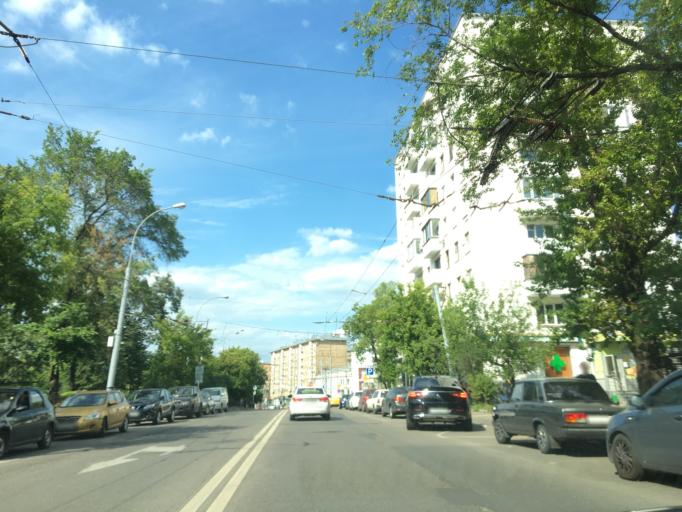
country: RU
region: Moskovskaya
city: Dorogomilovo
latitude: 55.7616
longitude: 37.5621
